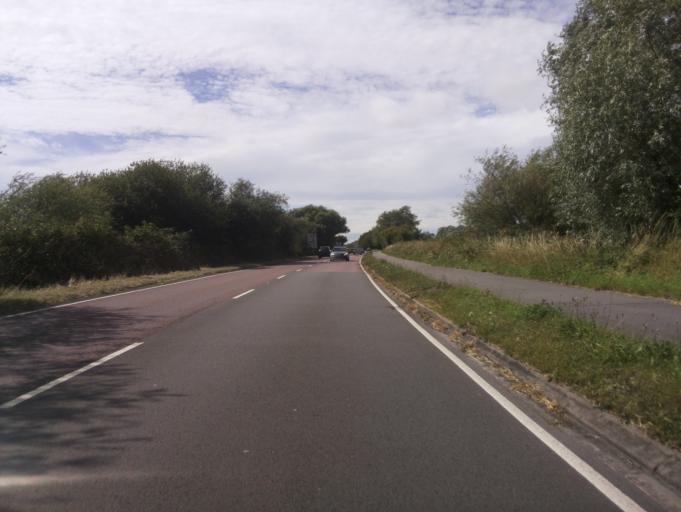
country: GB
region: England
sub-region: Dorset
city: Dorchester
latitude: 50.7231
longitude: -2.4553
